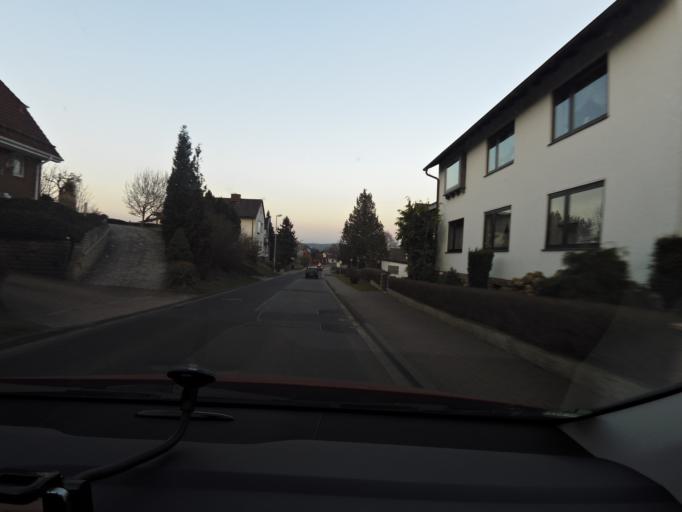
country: DE
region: Hesse
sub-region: Regierungsbezirk Kassel
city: Grossalmerode
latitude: 51.3291
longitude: 9.7801
